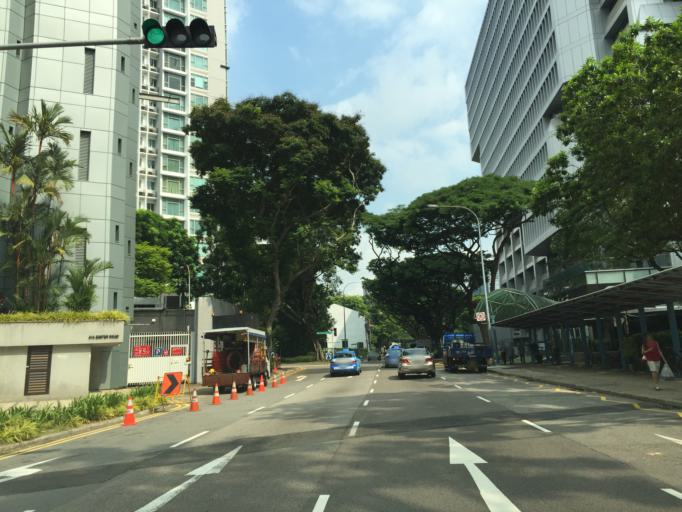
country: SG
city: Singapore
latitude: 1.2996
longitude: 103.8380
